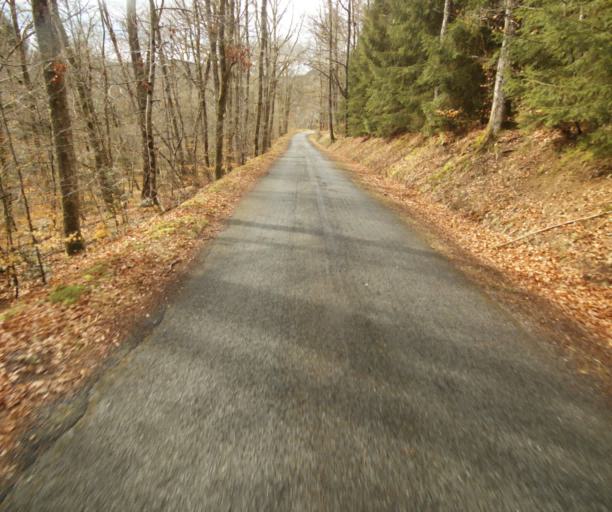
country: FR
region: Limousin
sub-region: Departement de la Correze
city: Saint-Privat
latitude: 45.2460
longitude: 1.9989
